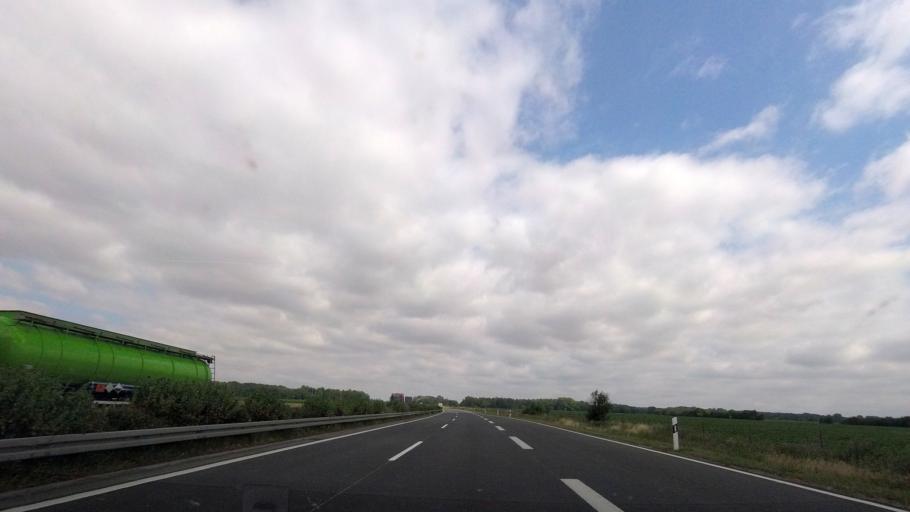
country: DE
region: Mecklenburg-Vorpommern
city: Jarmen
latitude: 53.9504
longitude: 13.3685
